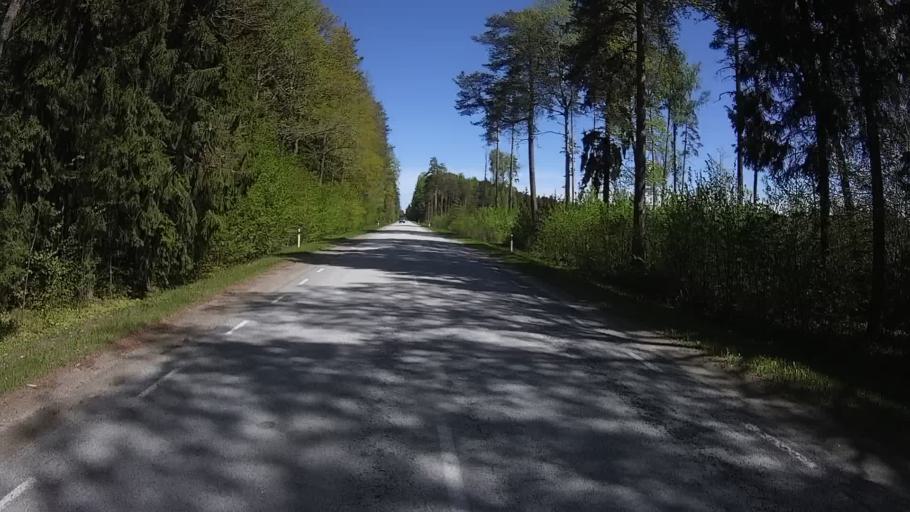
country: EE
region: Polvamaa
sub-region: Raepina vald
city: Rapina
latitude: 58.0778
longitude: 27.4269
